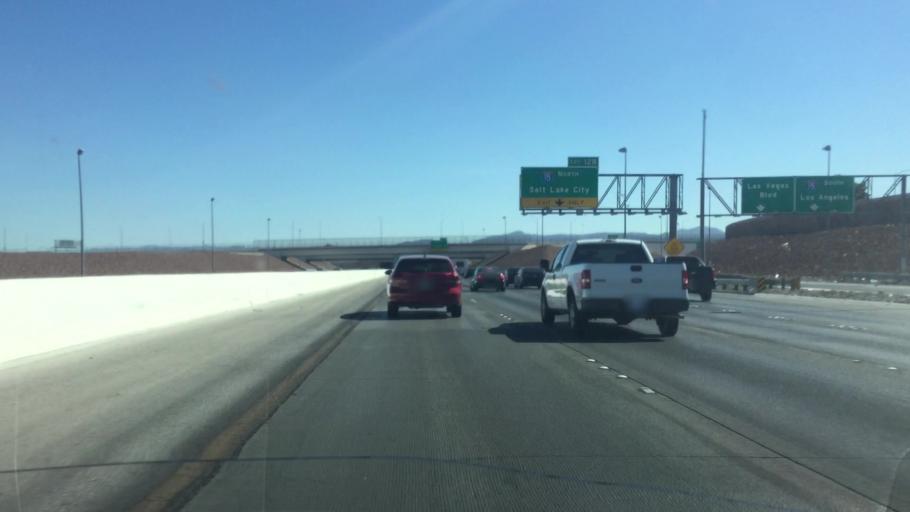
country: US
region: Nevada
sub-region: Clark County
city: Paradise
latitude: 36.0655
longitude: -115.1875
